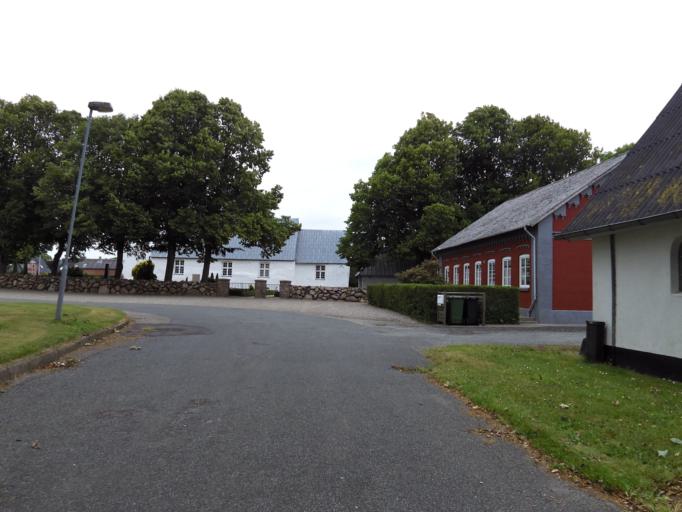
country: DK
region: South Denmark
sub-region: Tonder Kommune
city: Logumkloster
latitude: 55.1486
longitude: 8.9618
